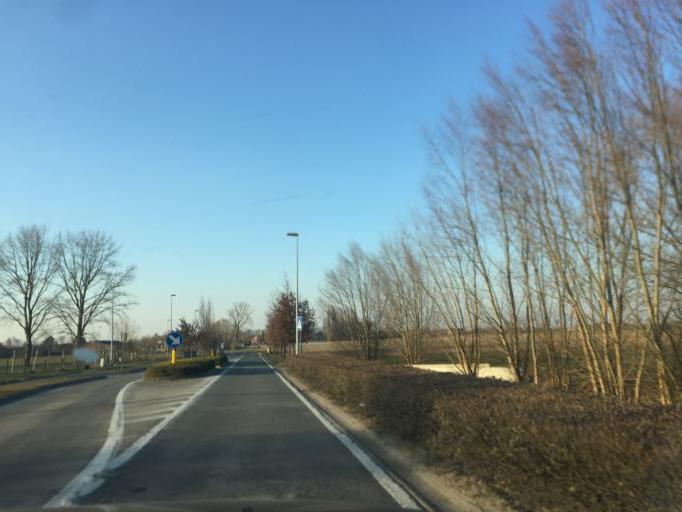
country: BE
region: Flanders
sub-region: Provincie West-Vlaanderen
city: Oostrozebeke
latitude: 50.9233
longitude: 3.3276
